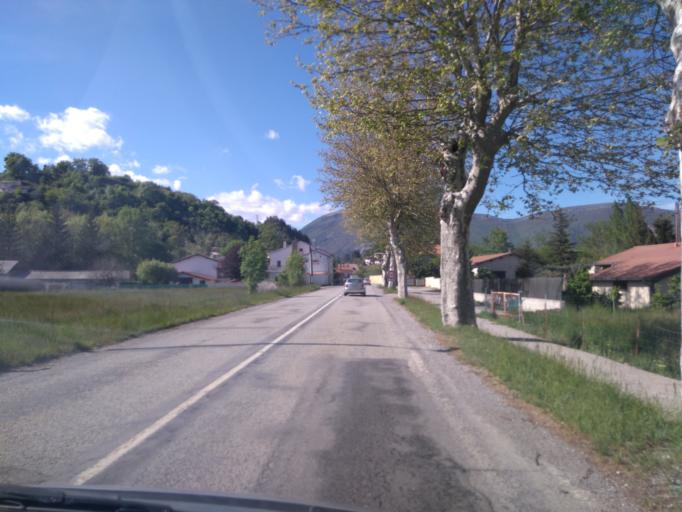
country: FR
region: Provence-Alpes-Cote d'Azur
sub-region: Departement des Hautes-Alpes
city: Serres
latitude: 44.4897
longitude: 5.7290
